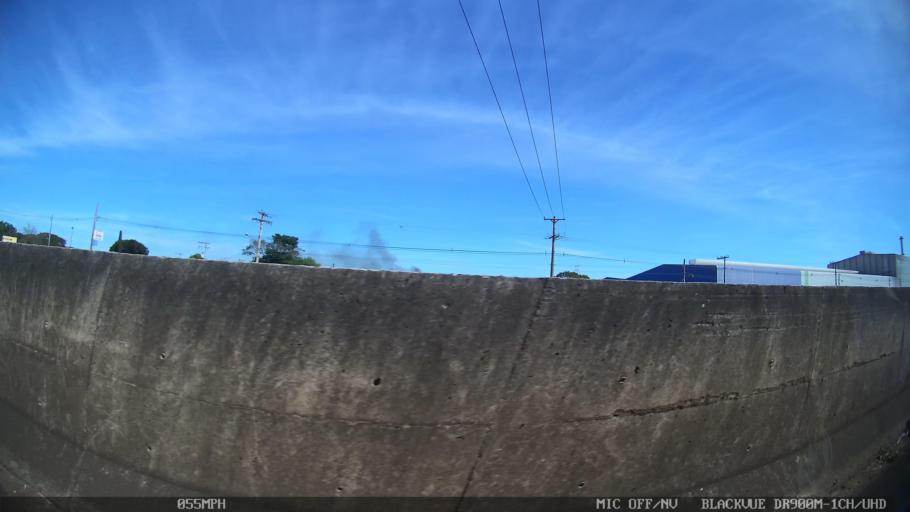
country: BR
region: Sao Paulo
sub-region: Porto Ferreira
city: Porto Ferreira
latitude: -21.8595
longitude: -47.4929
